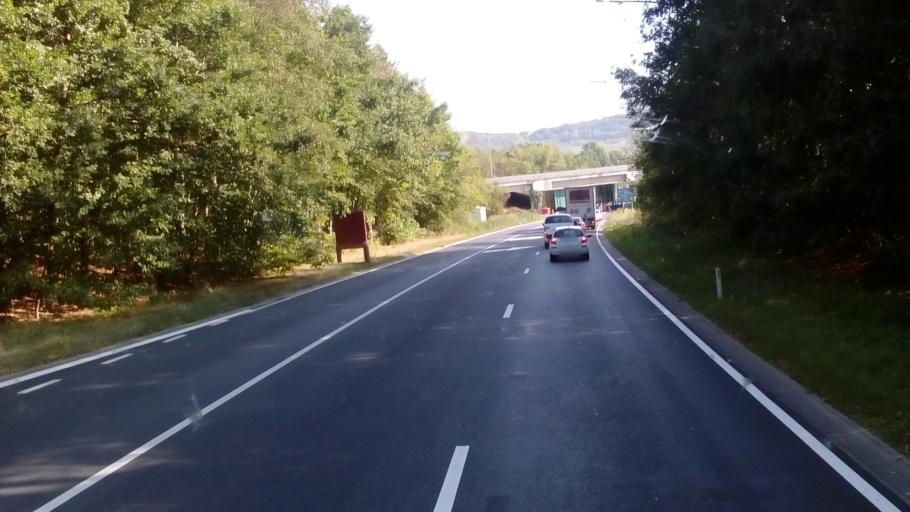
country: BE
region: Wallonia
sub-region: Province du Luxembourg
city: Aubange
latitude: 49.5548
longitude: 5.8083
